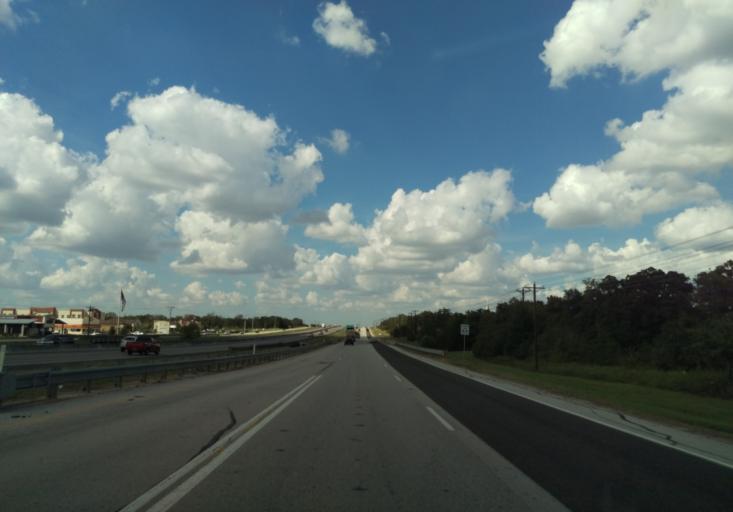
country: US
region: Texas
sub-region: Brazos County
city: College Station
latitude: 30.5630
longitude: -96.2623
